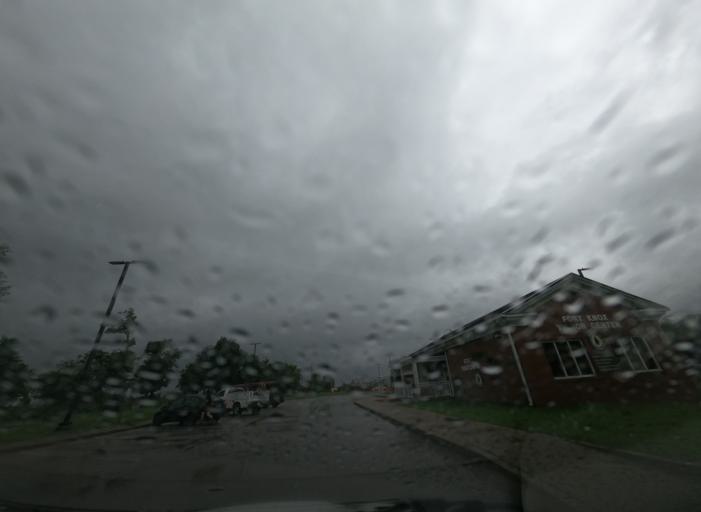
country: US
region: Kentucky
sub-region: Hardin County
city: Fort Knox
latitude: 37.8844
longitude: -85.9611
